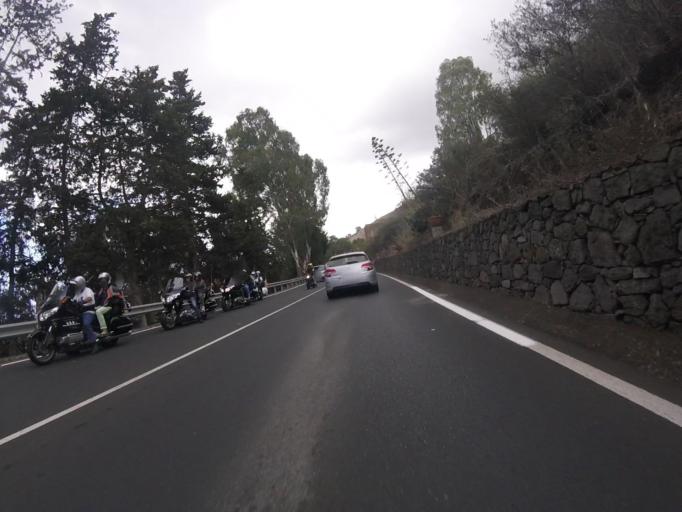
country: ES
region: Canary Islands
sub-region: Provincia de Las Palmas
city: Vega de San Mateo
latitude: 28.0177
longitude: -15.5236
